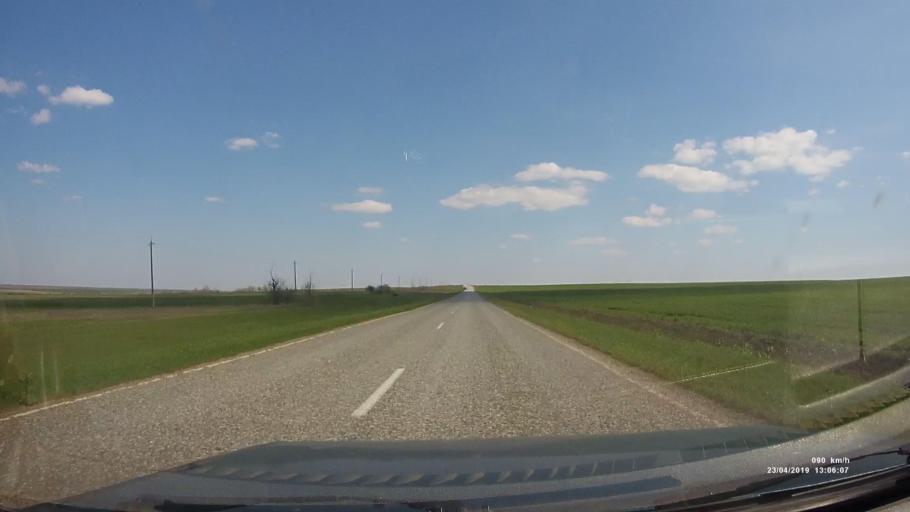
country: RU
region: Kalmykiya
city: Yashalta
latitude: 46.5918
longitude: 42.7352
